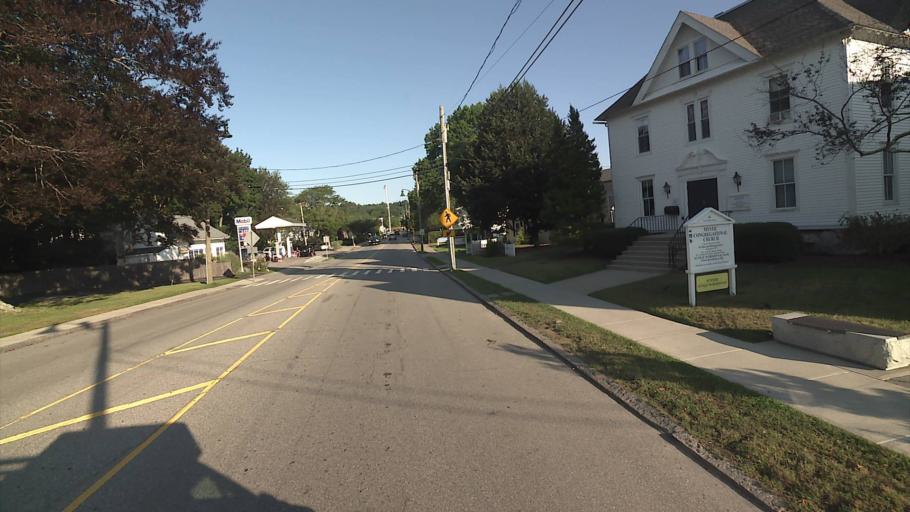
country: US
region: Connecticut
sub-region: New London County
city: Mystic
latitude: 41.3531
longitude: -71.9643
